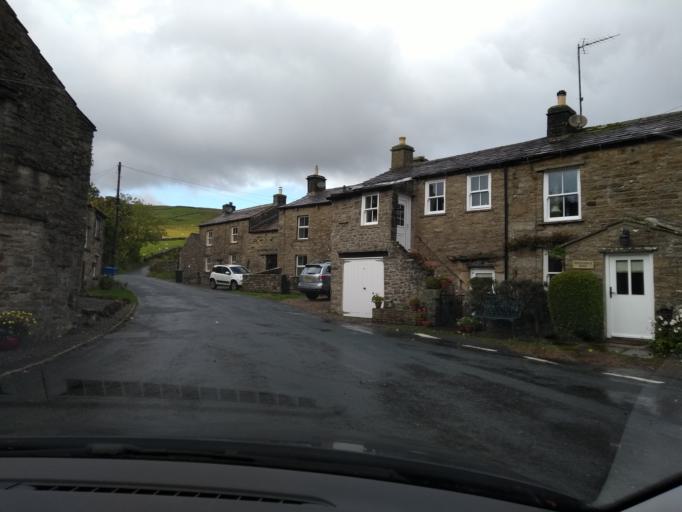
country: GB
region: England
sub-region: Cumbria
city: Kirkby Stephen
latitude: 54.3792
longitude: -2.1680
